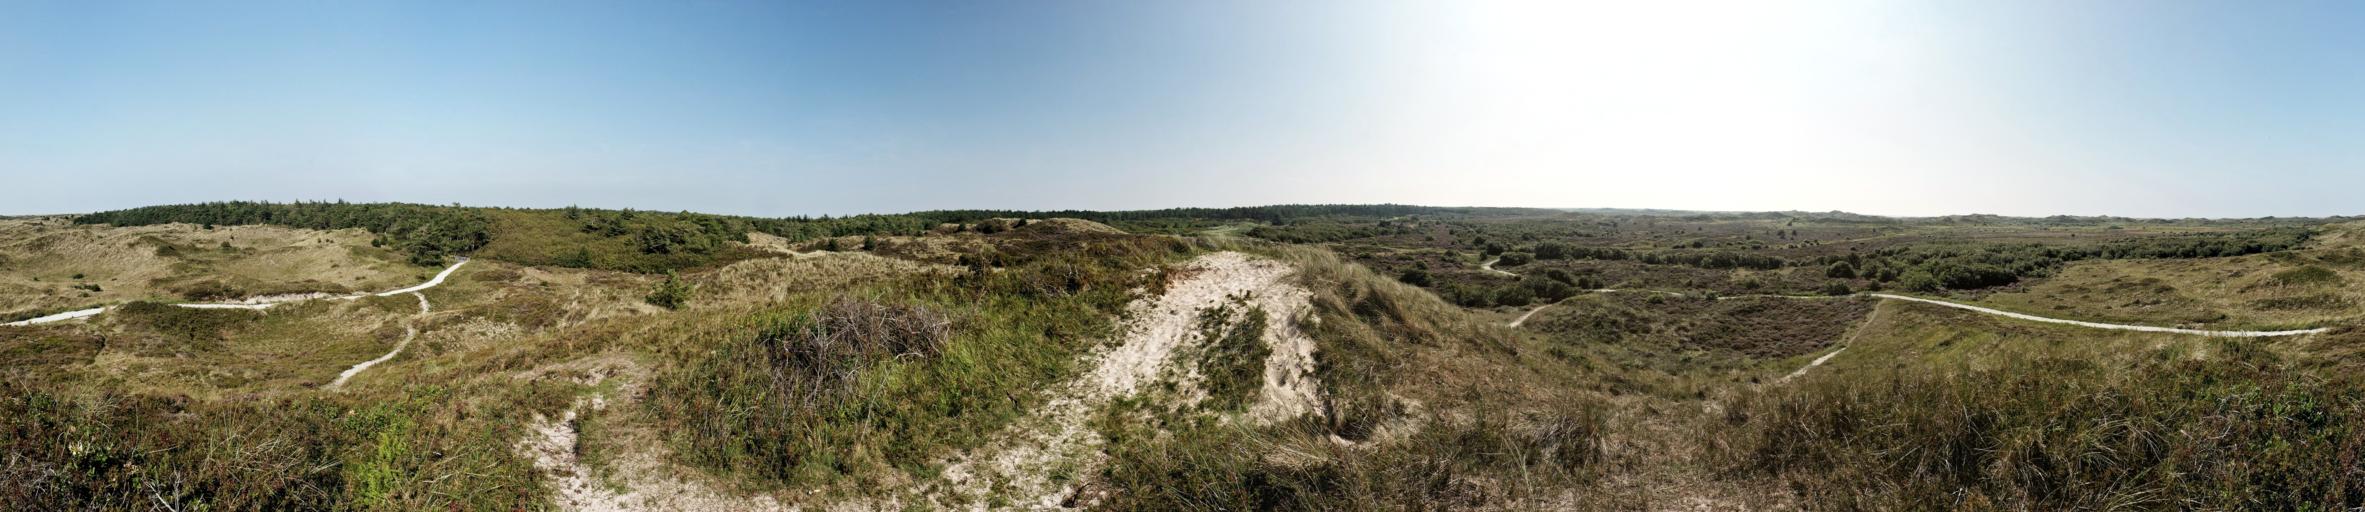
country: NL
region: North Holland
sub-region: Gemeente Texel
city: Den Burg
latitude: 53.0649
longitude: 4.7385
